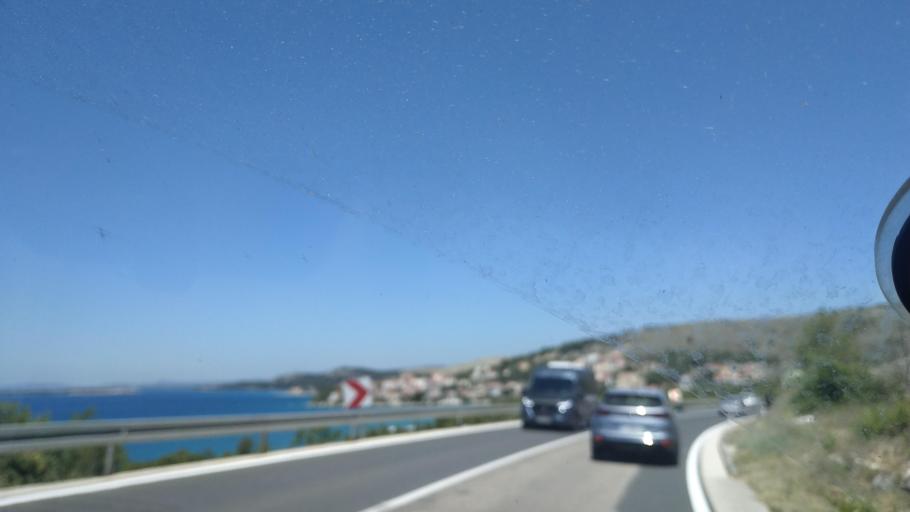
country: HR
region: Sibensko-Kniniska
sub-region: Grad Sibenik
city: Brodarica
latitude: 43.6473
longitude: 15.9507
